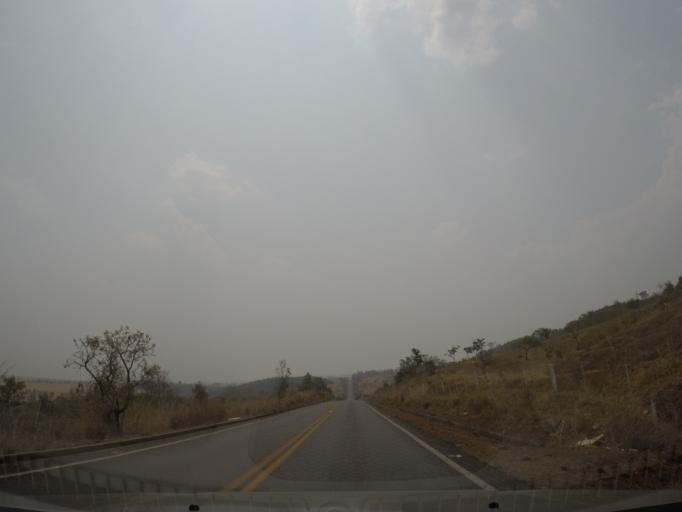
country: BR
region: Goias
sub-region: Pirenopolis
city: Pirenopolis
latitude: -15.9246
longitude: -48.8528
